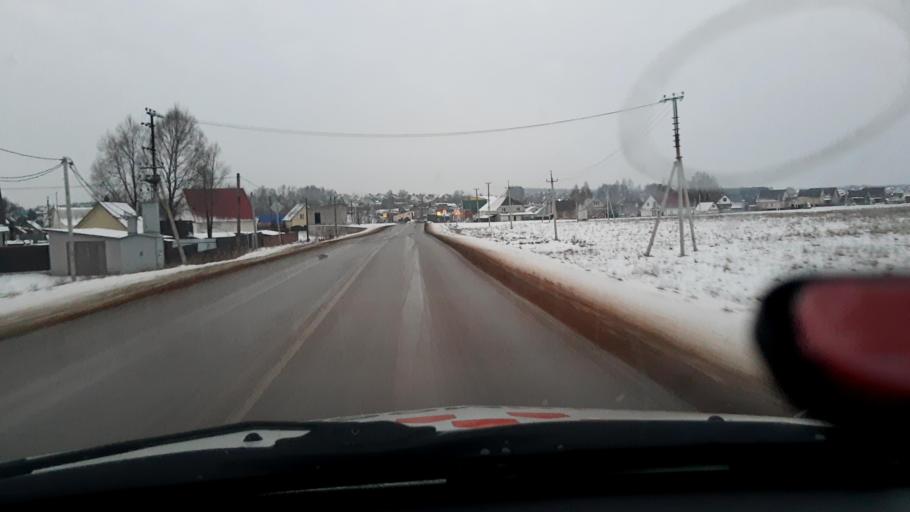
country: RU
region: Bashkortostan
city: Iglino
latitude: 54.8454
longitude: 56.4529
